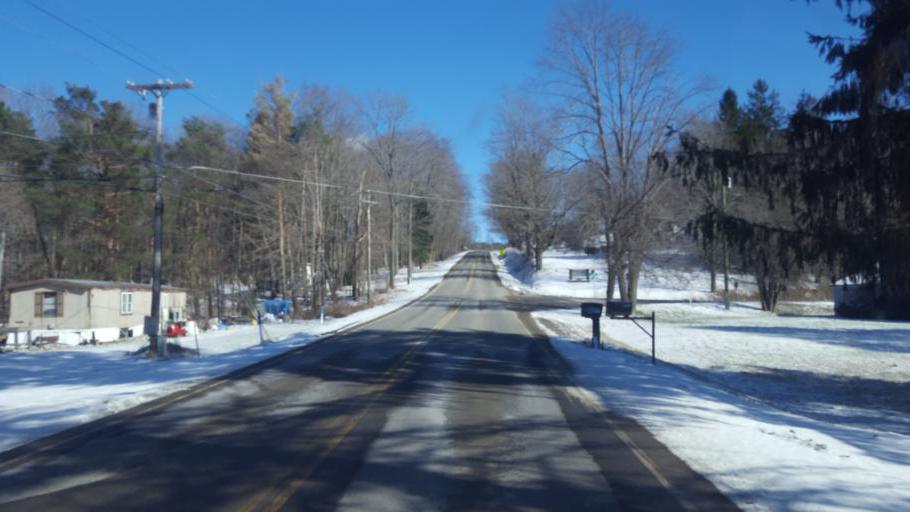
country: US
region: New York
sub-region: Allegany County
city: Friendship
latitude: 42.2059
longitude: -78.1233
